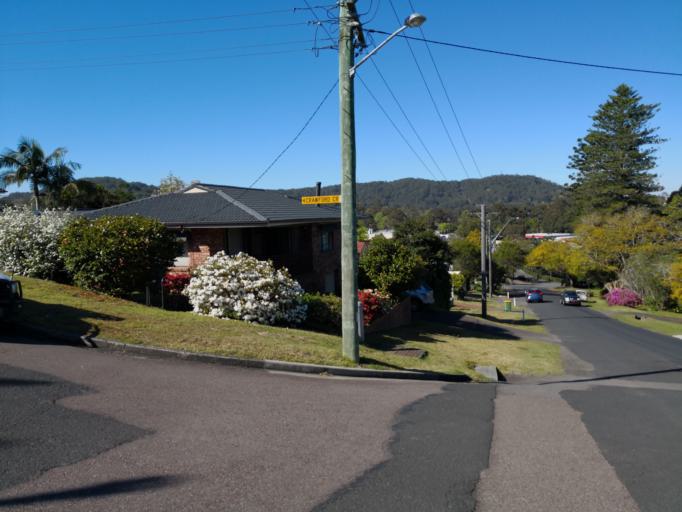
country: AU
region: New South Wales
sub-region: Gosford Shire
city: Narara
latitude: -33.4013
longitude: 151.3505
